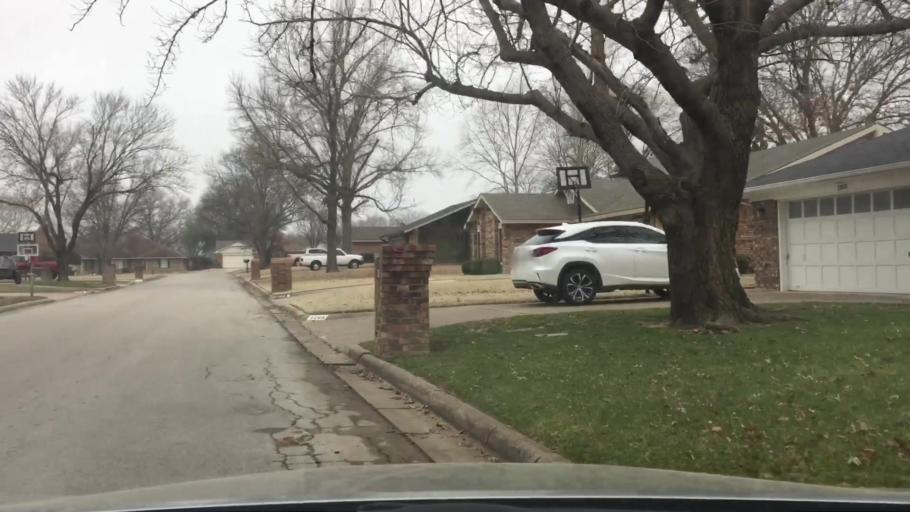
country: US
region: Oklahoma
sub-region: Carter County
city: Ardmore
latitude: 34.1580
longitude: -97.1473
